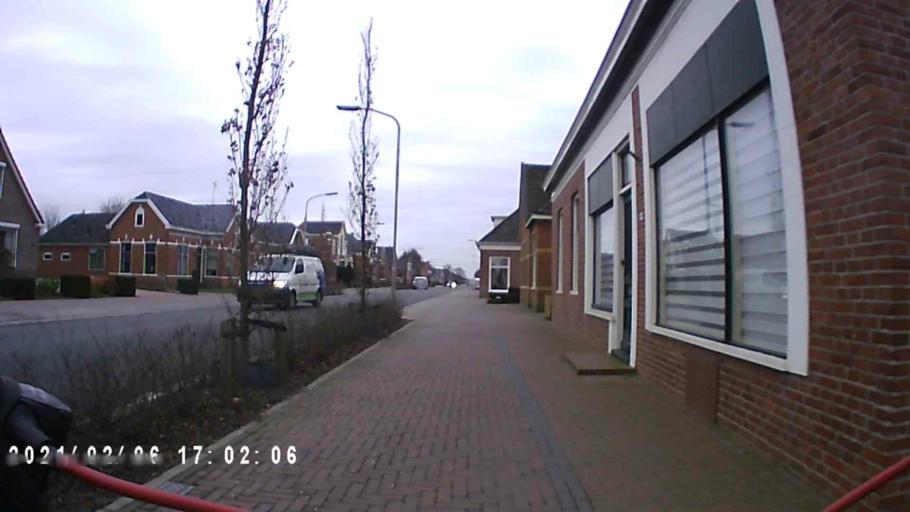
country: NL
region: Groningen
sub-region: Gemeente Appingedam
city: Appingedam
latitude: 53.4201
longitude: 6.7649
